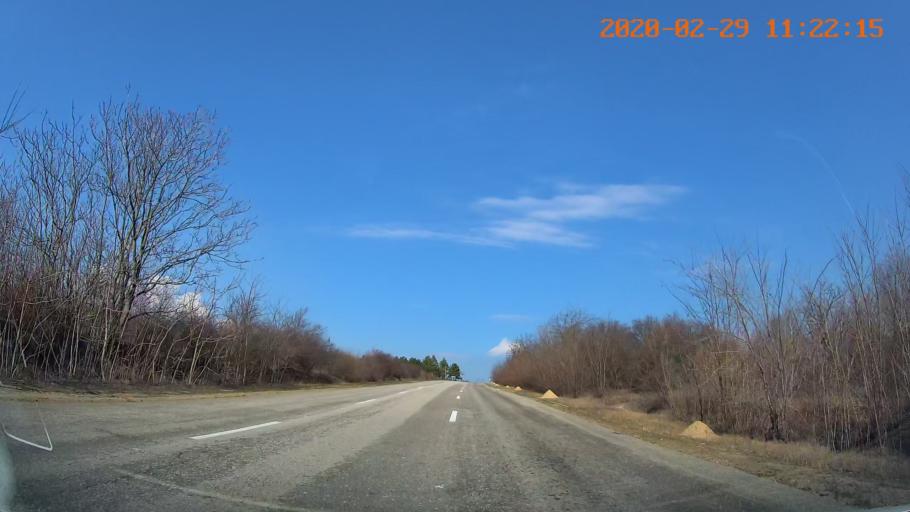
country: MD
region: Telenesti
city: Cocieri
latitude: 47.3916
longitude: 29.1631
